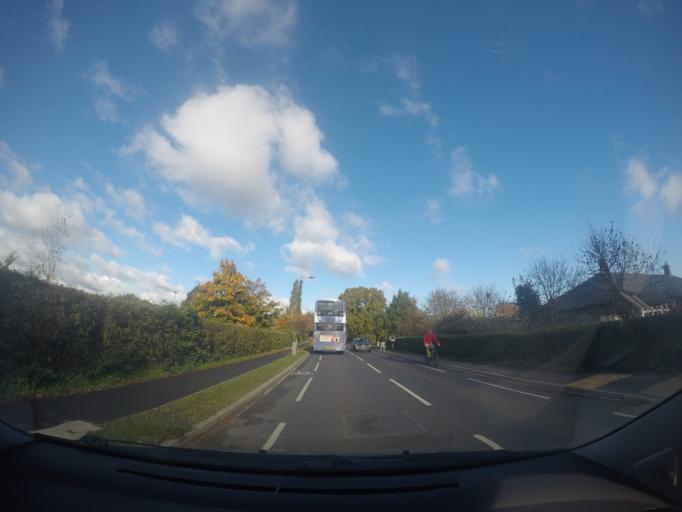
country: GB
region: England
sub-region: City of York
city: Haxby
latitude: 53.9962
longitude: -1.0716
